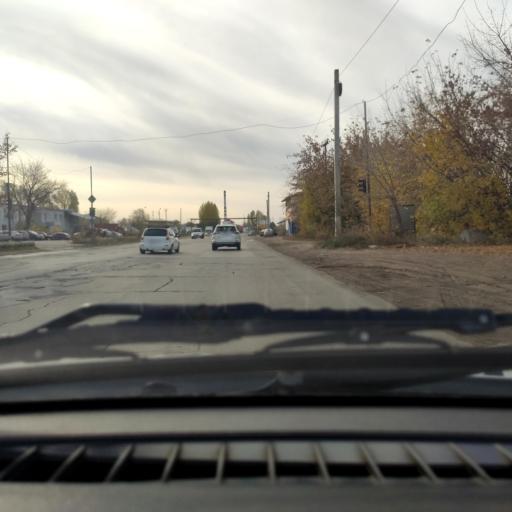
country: RU
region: Samara
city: Tol'yatti
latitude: 53.5255
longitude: 49.4714
